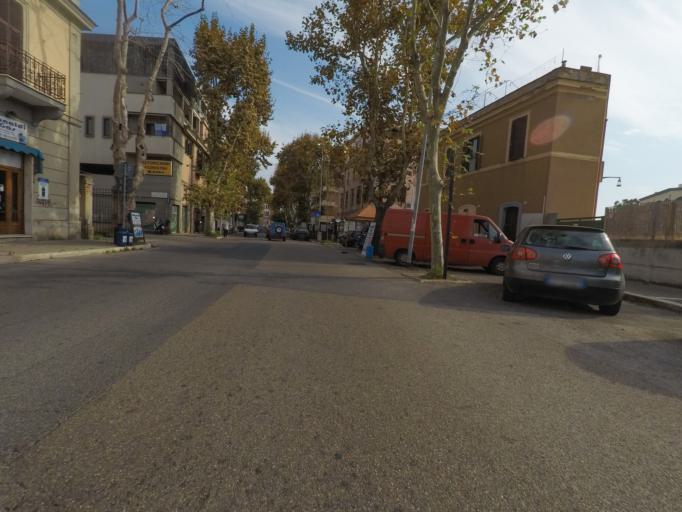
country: IT
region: Latium
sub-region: Citta metropolitana di Roma Capitale
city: Civitavecchia
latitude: 42.0942
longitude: 11.7955
